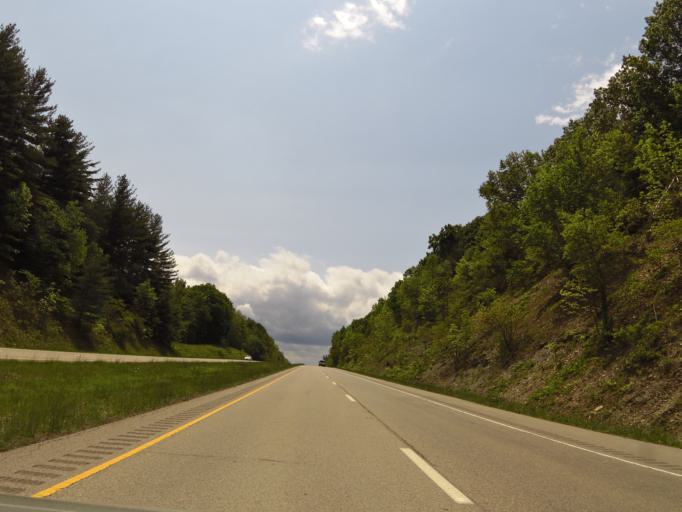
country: US
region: Ohio
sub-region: Meigs County
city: Pomeroy
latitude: 39.0922
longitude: -82.0146
